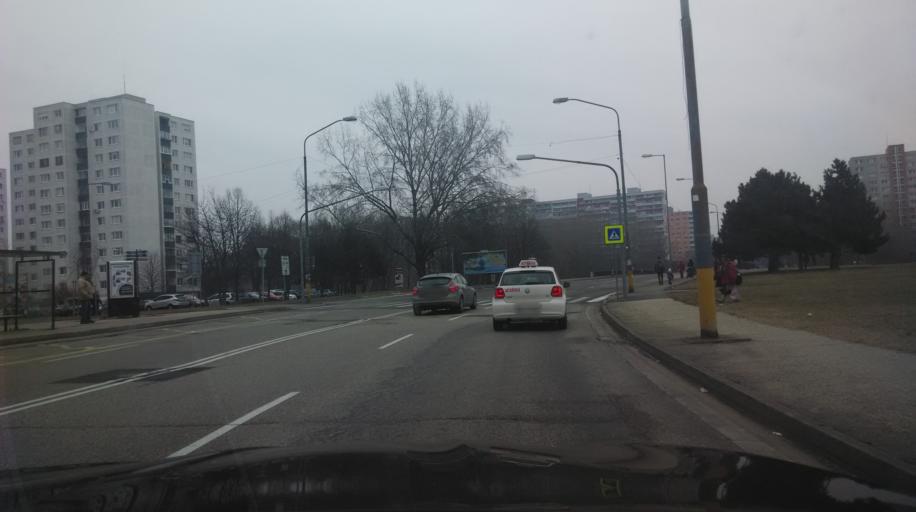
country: SK
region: Bratislavsky
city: Bratislava
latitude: 48.1174
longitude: 17.1051
